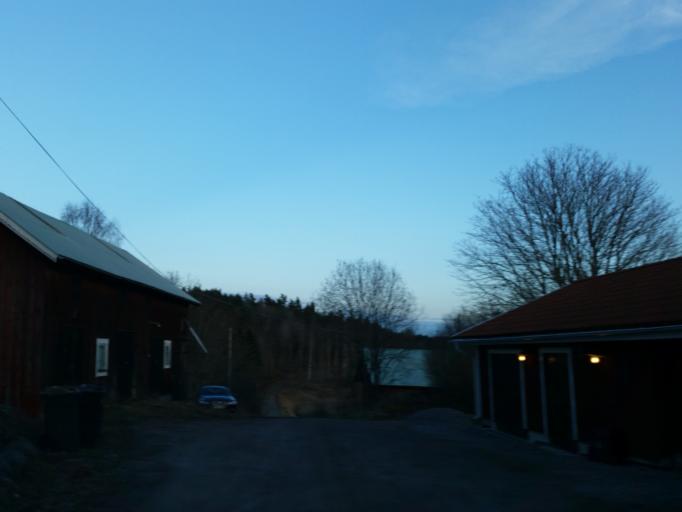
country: SE
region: Kalmar
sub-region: Vasterviks Kommun
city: Ankarsrum
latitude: 57.7096
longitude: 16.4628
